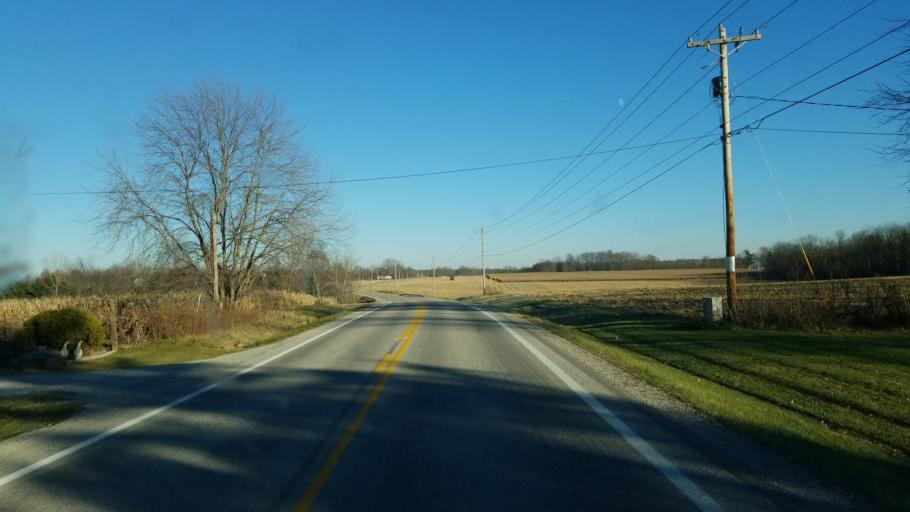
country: US
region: Ohio
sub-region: Delaware County
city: Ashley
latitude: 40.4063
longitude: -82.8814
